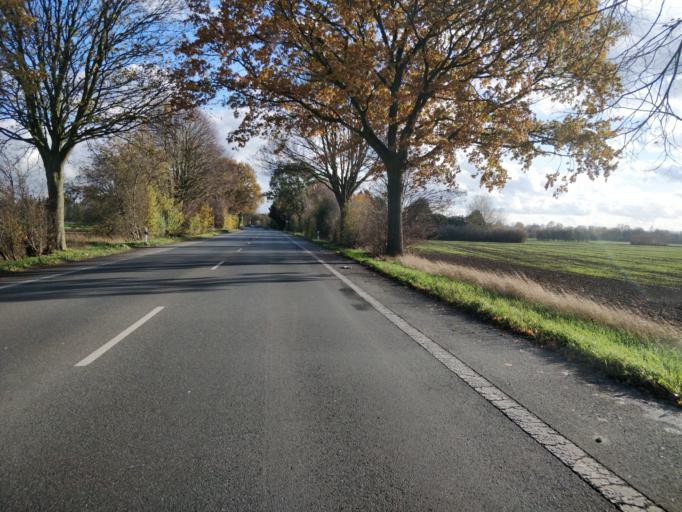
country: DE
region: North Rhine-Westphalia
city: Rees
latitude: 51.7721
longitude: 6.3860
